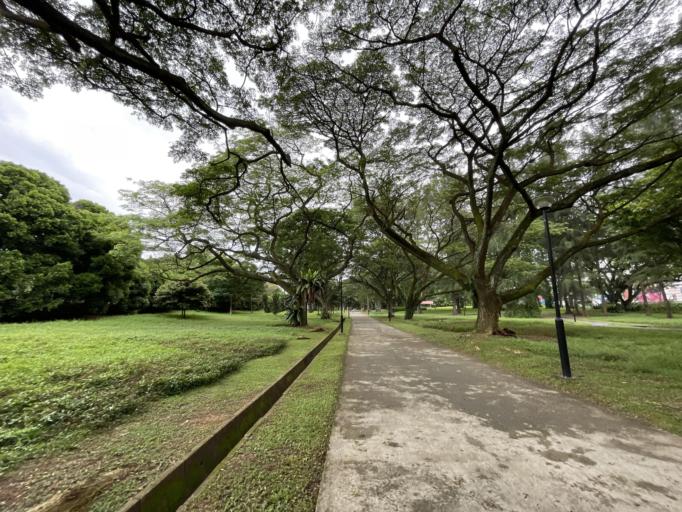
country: SG
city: Singapore
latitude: 1.2904
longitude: 103.7686
